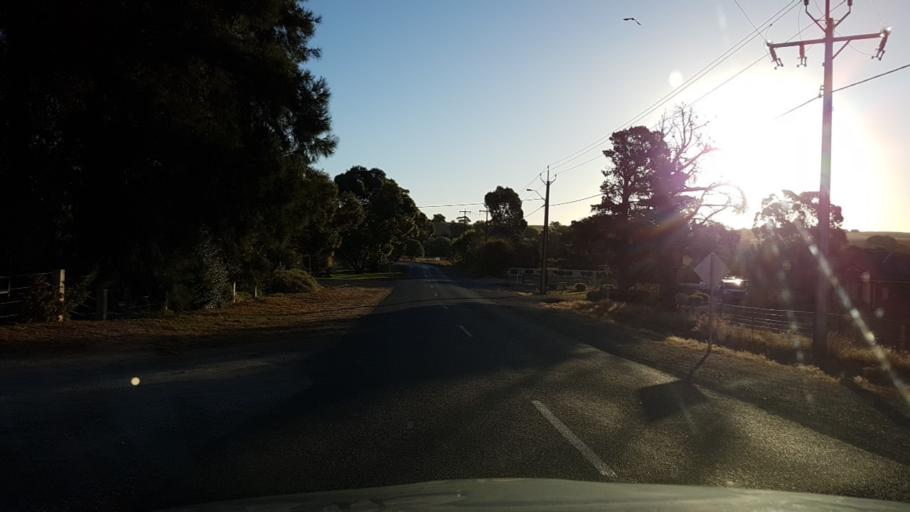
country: AU
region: South Australia
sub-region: Clare and Gilbert Valleys
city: Clare
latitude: -34.0227
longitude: 138.6898
